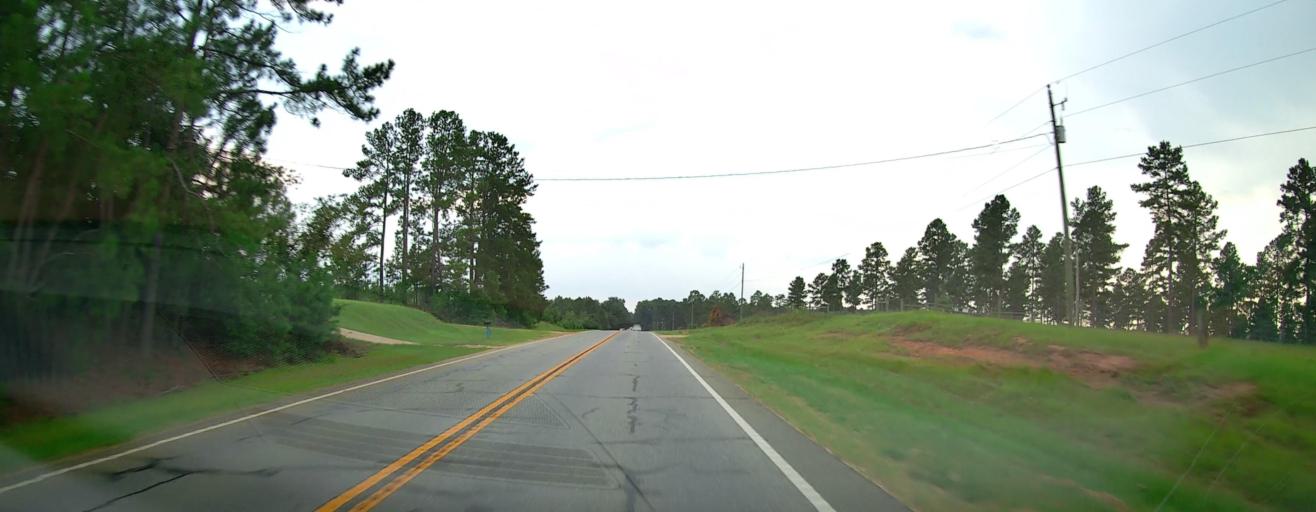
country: US
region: Georgia
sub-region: Laurens County
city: East Dublin
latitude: 32.5899
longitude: -82.8310
